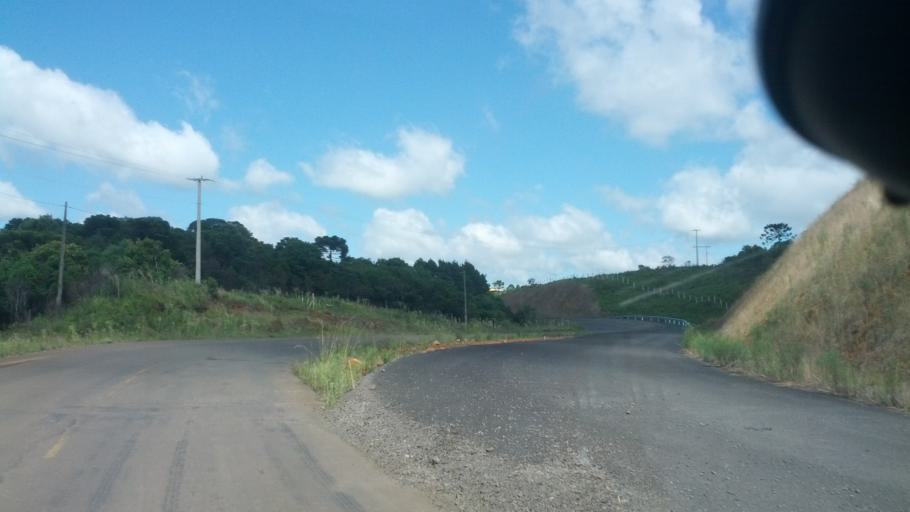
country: BR
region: Santa Catarina
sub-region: Lages
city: Lages
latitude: -27.9504
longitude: -50.4985
